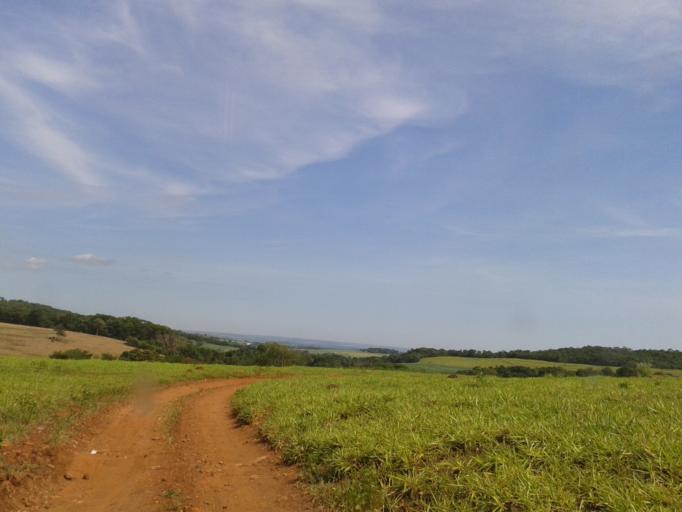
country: BR
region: Minas Gerais
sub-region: Centralina
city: Centralina
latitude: -18.6984
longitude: -49.2082
